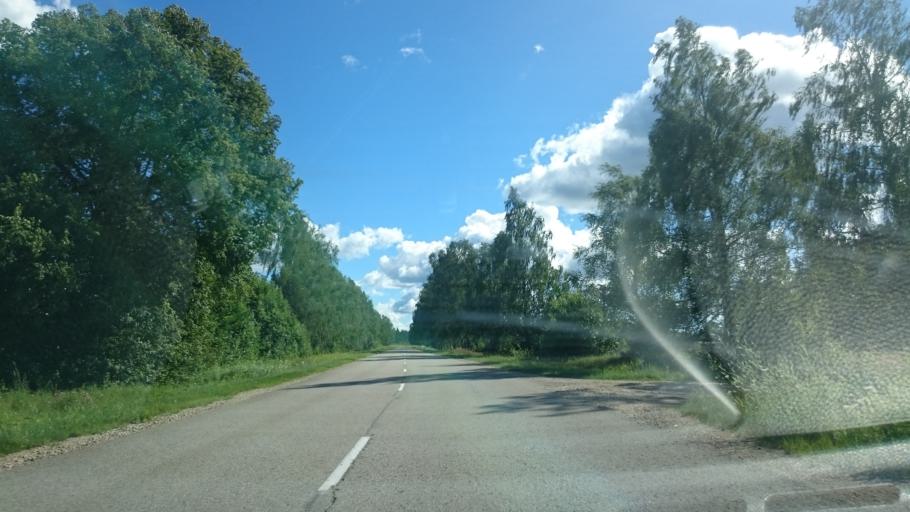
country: LV
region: Kuldigas Rajons
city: Kuldiga
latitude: 56.8990
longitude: 21.8892
